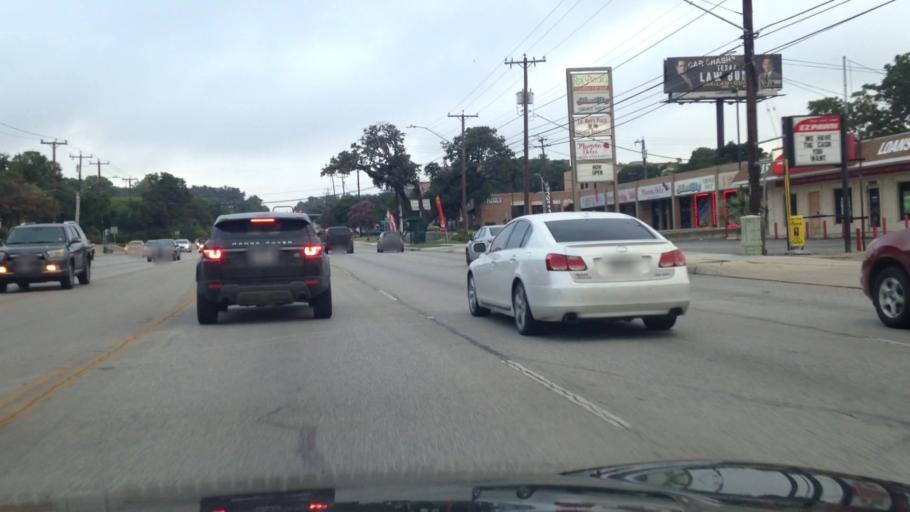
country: US
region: Texas
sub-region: Bexar County
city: Balcones Heights
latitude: 29.5037
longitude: -98.5610
